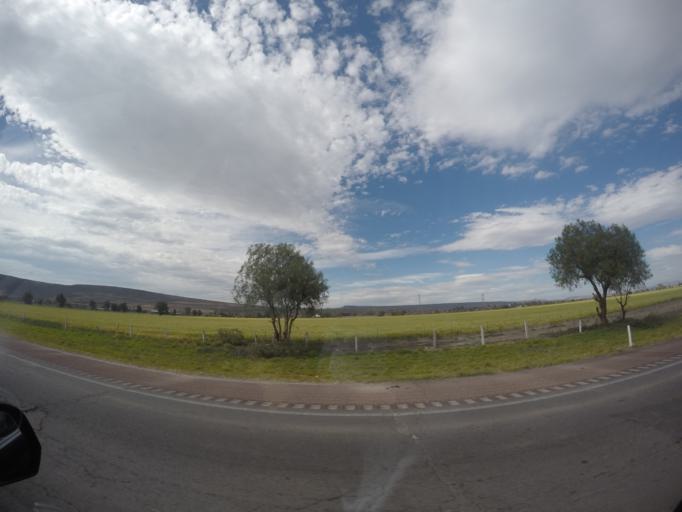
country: MX
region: Guanajuato
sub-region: Salamanca
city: San Jose de la Montana
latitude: 20.5886
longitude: -101.0661
